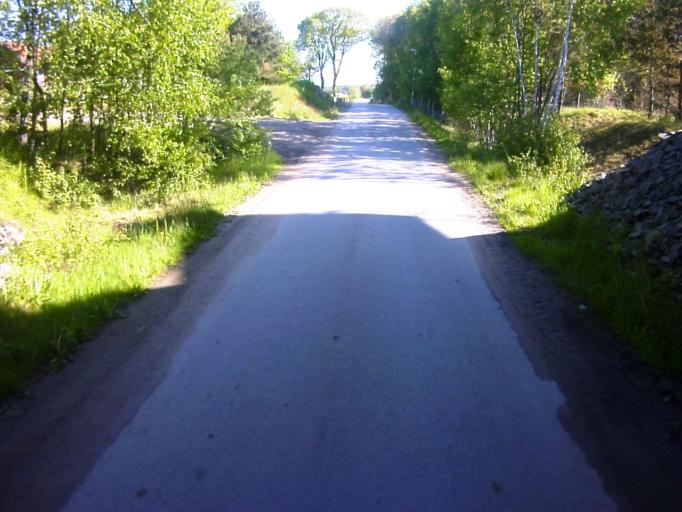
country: SE
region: Blekinge
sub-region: Solvesborgs Kommun
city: Soelvesborg
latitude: 56.0652
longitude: 14.6094
